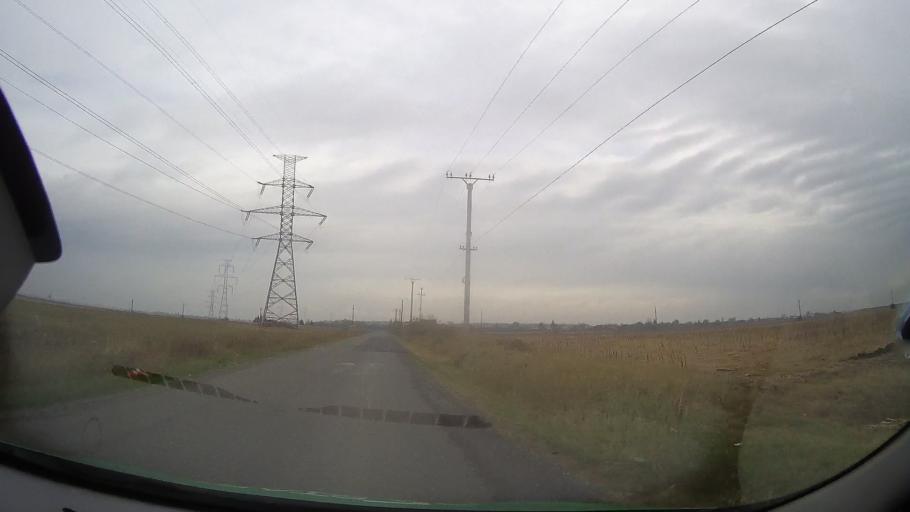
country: RO
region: Prahova
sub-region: Comuna Valea Calugareasca
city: Pantazi
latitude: 44.9268
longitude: 26.1516
